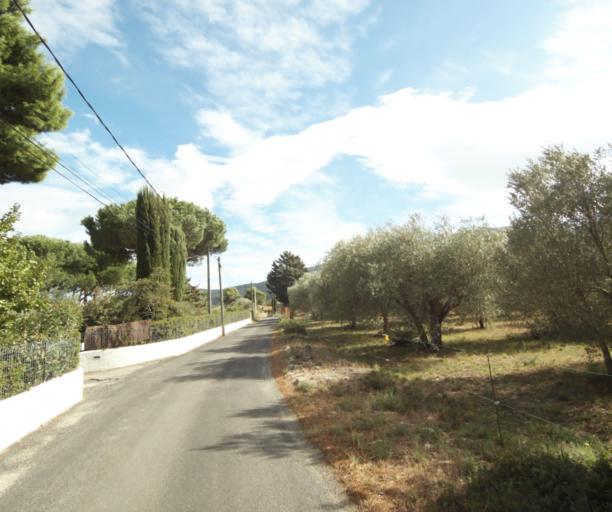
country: FR
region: Languedoc-Roussillon
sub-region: Departement des Pyrenees-Orientales
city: Argelers
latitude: 42.5396
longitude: 2.9960
